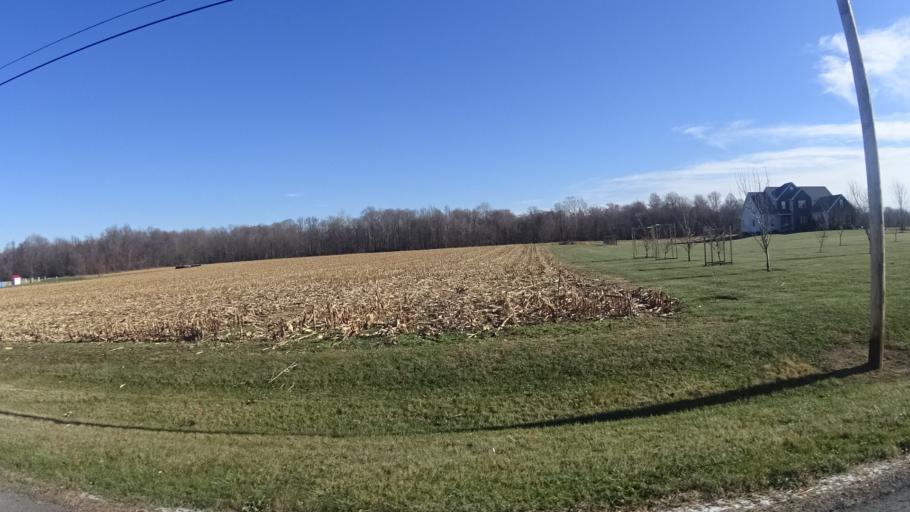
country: US
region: Ohio
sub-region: Lorain County
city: Vermilion
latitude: 41.3381
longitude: -82.3445
